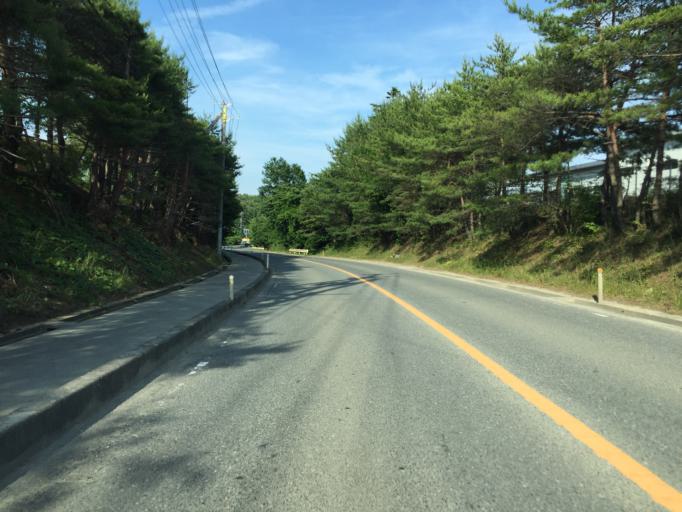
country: JP
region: Fukushima
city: Namie
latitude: 37.6690
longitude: 140.9884
